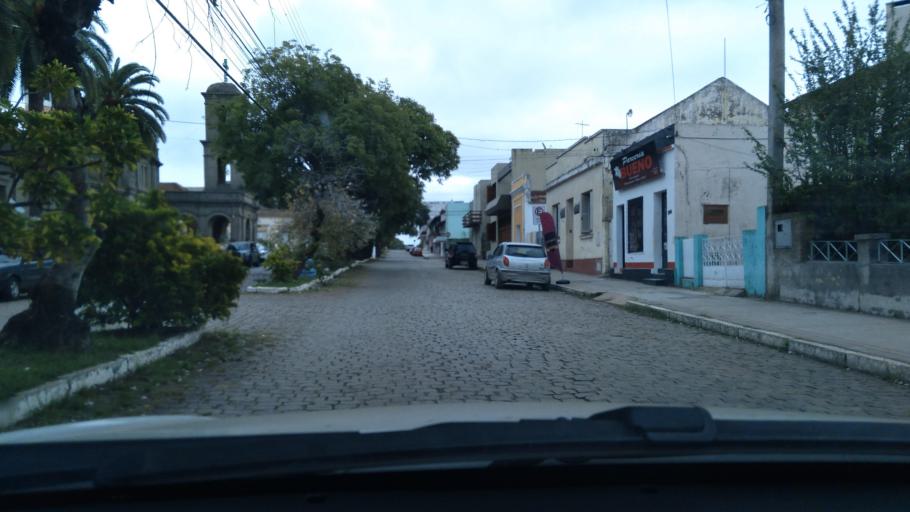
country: BR
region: Rio Grande do Sul
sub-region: Dom Pedrito
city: Dom Pedrito
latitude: -30.9851
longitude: -54.6719
